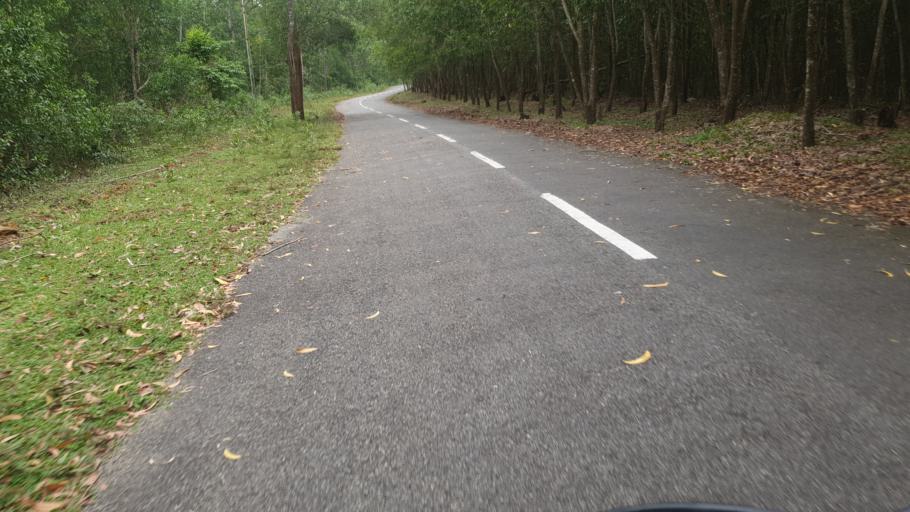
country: IN
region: Kerala
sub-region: Thiruvananthapuram
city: Nedumangad
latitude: 8.6319
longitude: 77.1204
